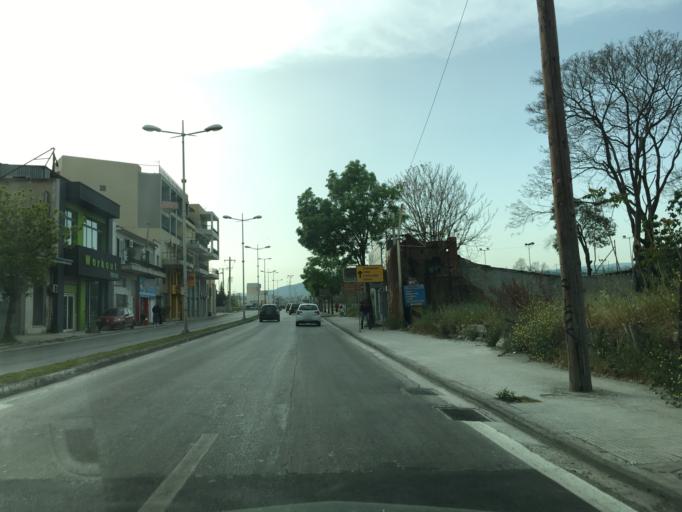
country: GR
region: Thessaly
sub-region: Nomos Magnisias
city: Nea Ionia
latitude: 39.3621
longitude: 22.9332
